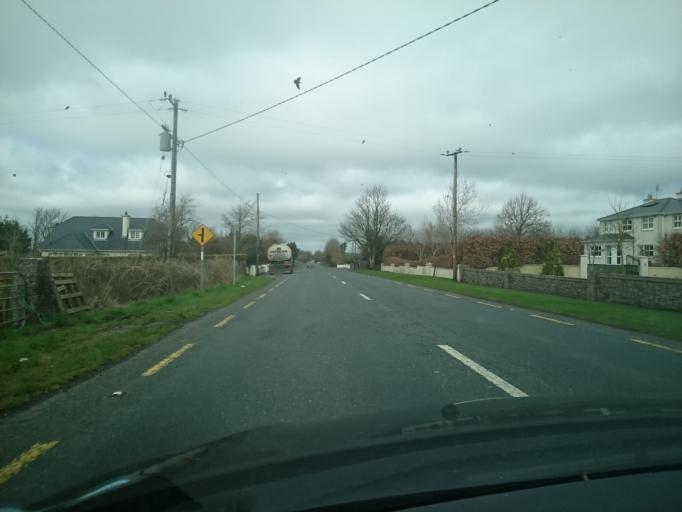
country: IE
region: Connaught
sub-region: Maigh Eo
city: Claremorris
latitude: 53.7443
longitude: -9.0185
